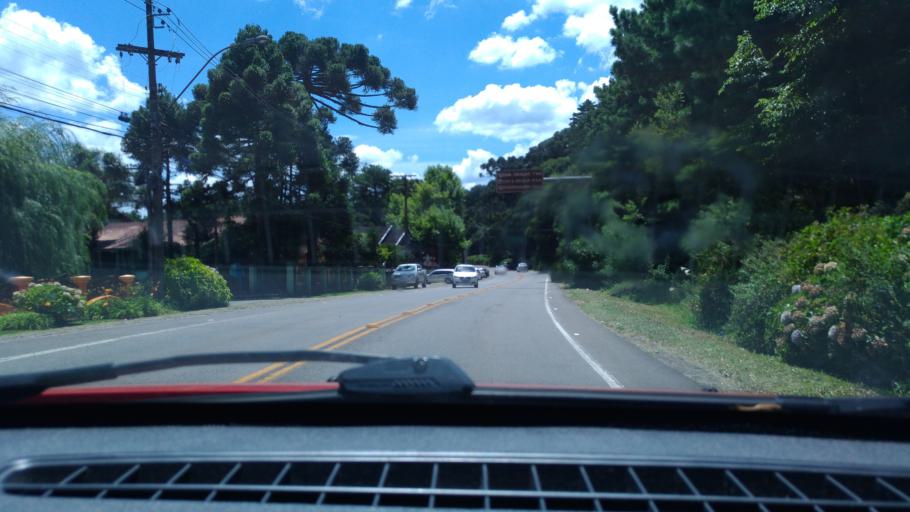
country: BR
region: Rio Grande do Sul
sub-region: Canela
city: Canela
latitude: -29.3577
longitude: -50.8278
